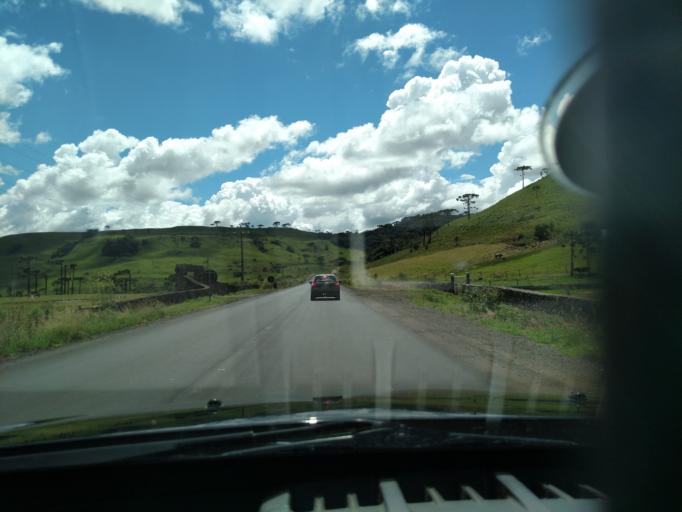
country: BR
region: Santa Catarina
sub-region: Sao Joaquim
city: Sao Joaquim
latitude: -28.2560
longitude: -49.9658
